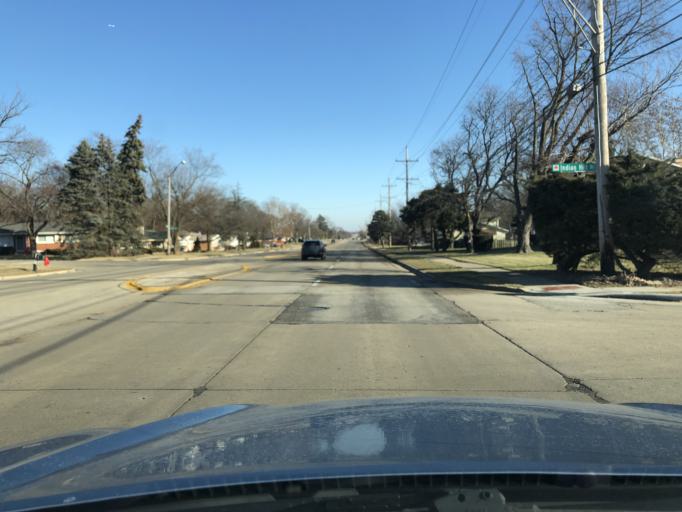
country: US
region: Illinois
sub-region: DuPage County
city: Roselle
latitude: 41.9980
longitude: -88.0781
